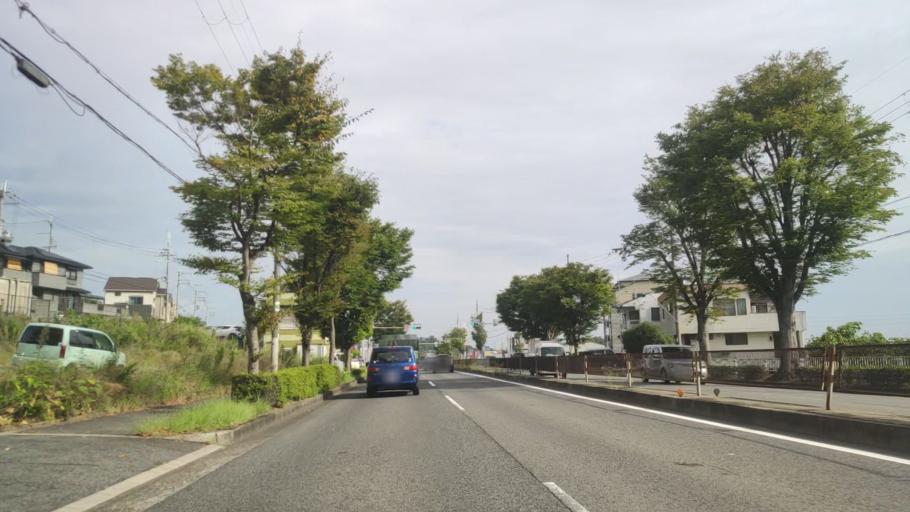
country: JP
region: Osaka
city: Tondabayashicho
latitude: 34.4717
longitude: 135.5755
